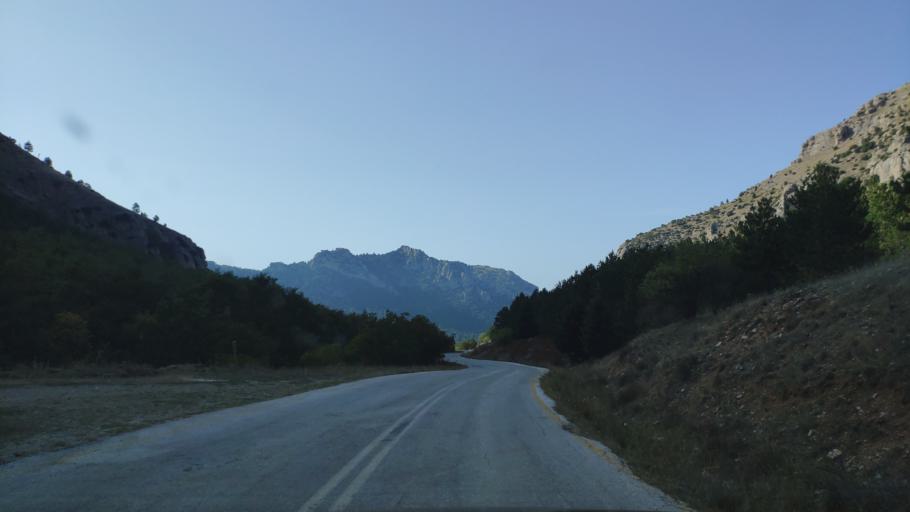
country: GR
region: West Greece
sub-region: Nomos Achaias
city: Aiyira
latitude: 38.0404
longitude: 22.3945
